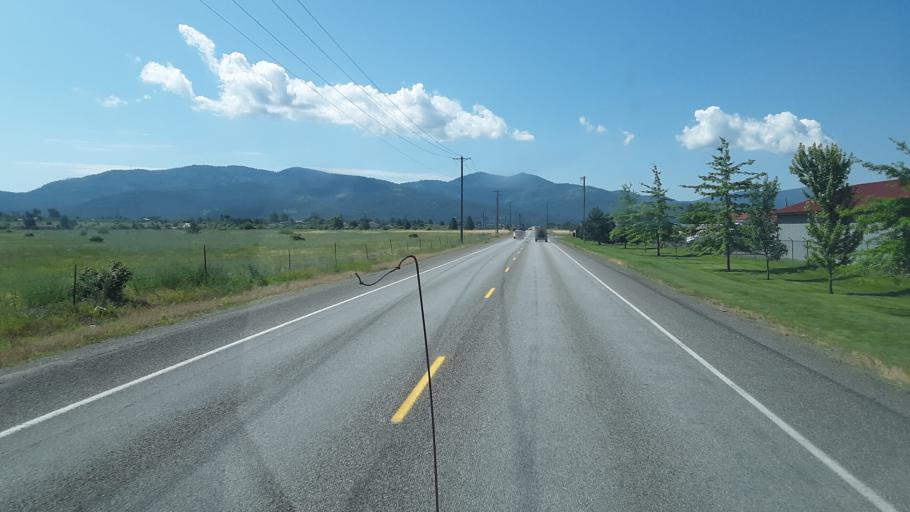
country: US
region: Idaho
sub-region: Kootenai County
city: Post Falls
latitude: 47.7362
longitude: -117.0019
